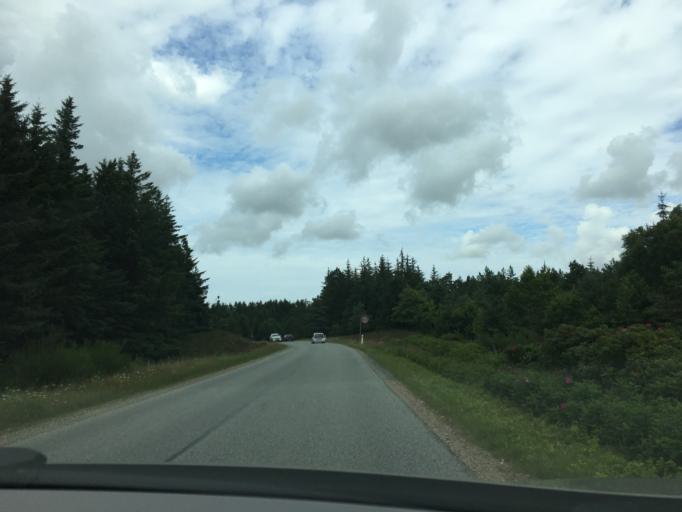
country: DK
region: South Denmark
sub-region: Varde Kommune
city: Oksbol
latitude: 55.7557
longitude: 8.2503
